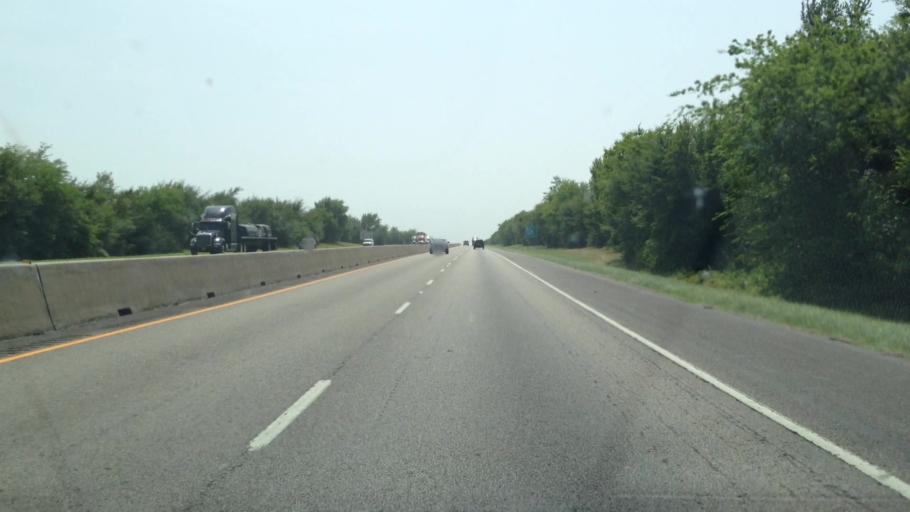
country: US
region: Texas
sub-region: Hopkins County
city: Sulphur Springs
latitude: 33.1596
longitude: -95.4132
